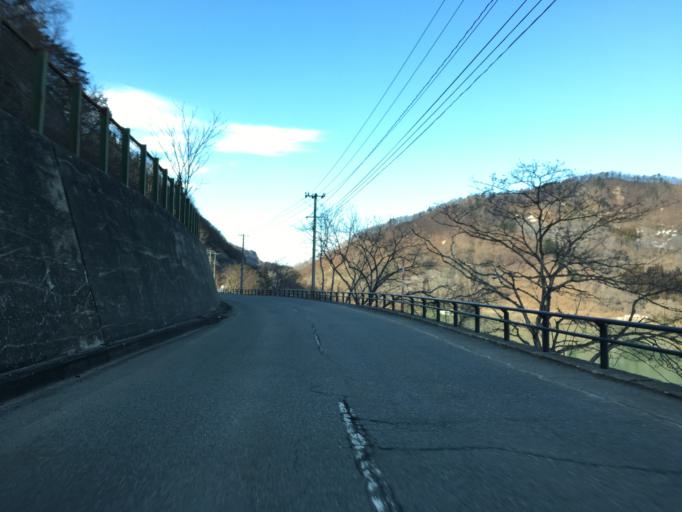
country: JP
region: Yamagata
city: Nagai
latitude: 37.9550
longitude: 139.9165
